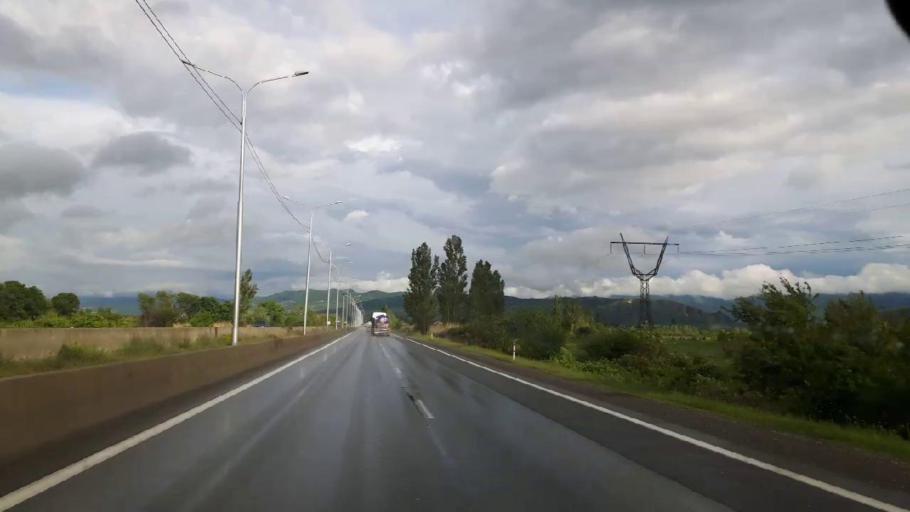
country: GE
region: Shida Kartli
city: Kaspi
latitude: 41.9238
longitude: 44.5413
